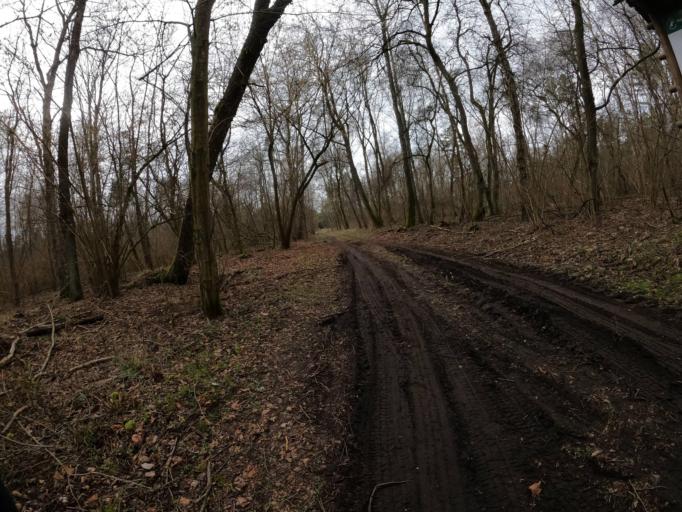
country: PL
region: Greater Poland Voivodeship
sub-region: Powiat zlotowski
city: Sypniewo
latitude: 53.4781
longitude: 16.5203
